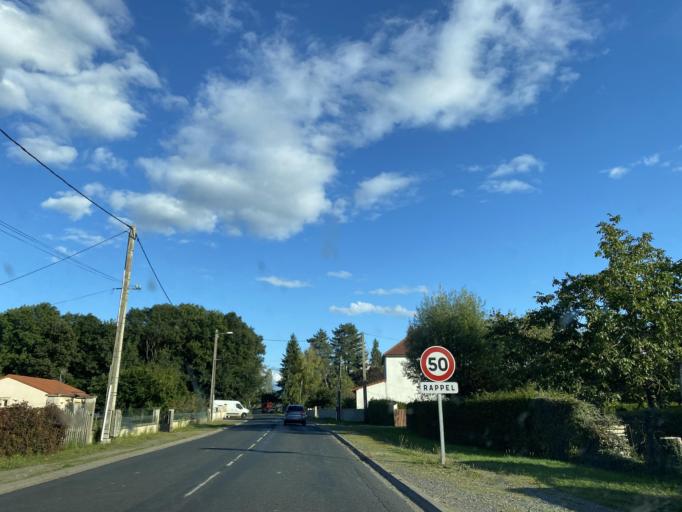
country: FR
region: Auvergne
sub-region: Departement du Puy-de-Dome
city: Randan
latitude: 46.0190
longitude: 3.3735
